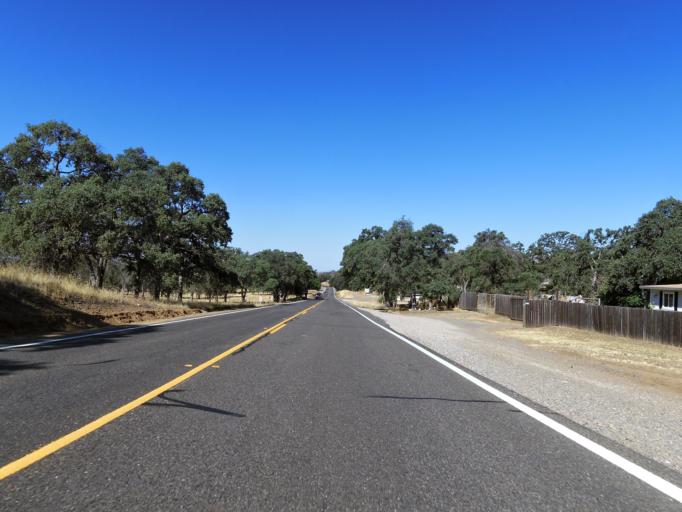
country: US
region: California
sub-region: Mariposa County
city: Mariposa
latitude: 37.4362
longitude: -120.0906
